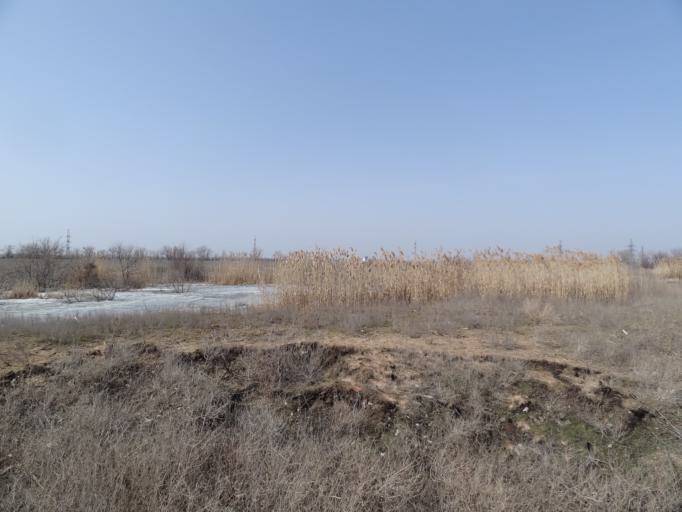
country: RU
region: Saratov
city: Engel's
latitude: 51.4227
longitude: 46.1791
